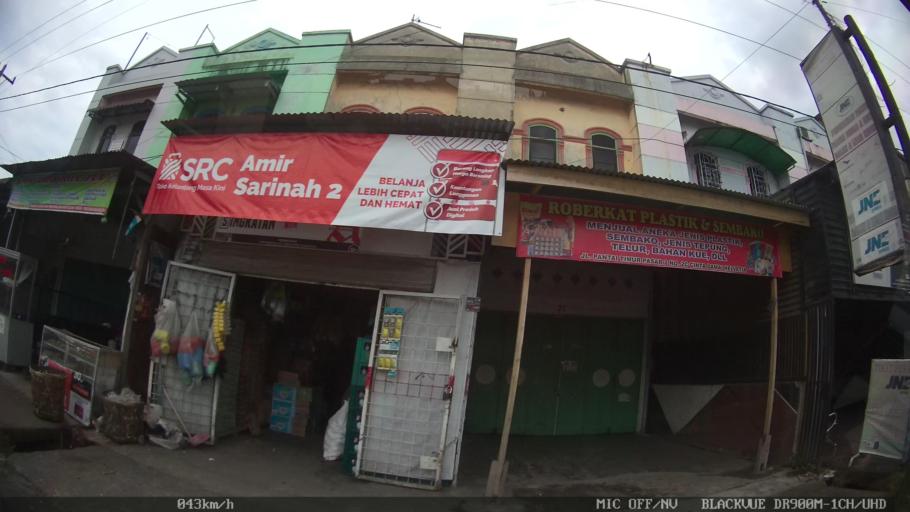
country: ID
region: North Sumatra
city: Sunggal
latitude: 3.5963
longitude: 98.6176
